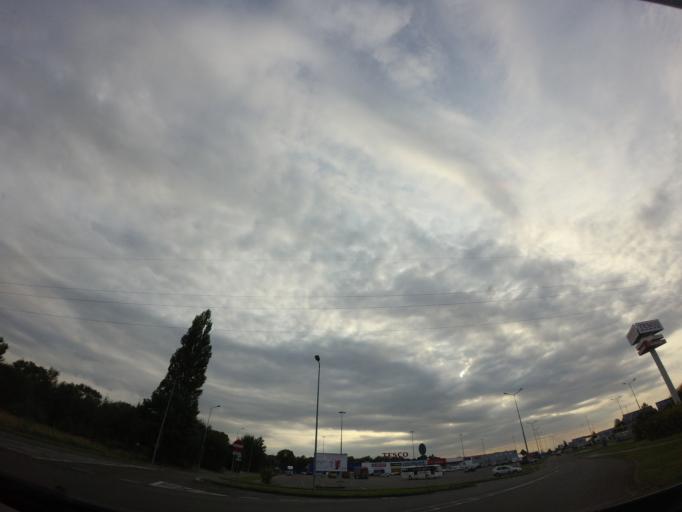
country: PL
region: West Pomeranian Voivodeship
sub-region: Powiat stargardzki
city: Stargard Szczecinski
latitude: 53.3421
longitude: 14.9932
